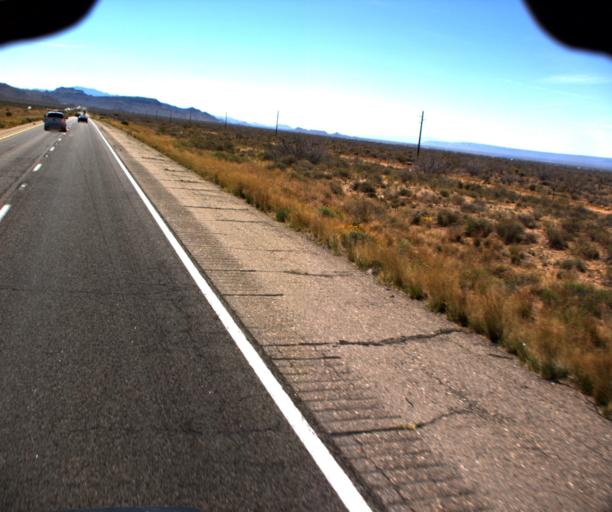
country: US
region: Arizona
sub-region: Mohave County
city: Golden Valley
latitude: 35.2888
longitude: -114.1814
